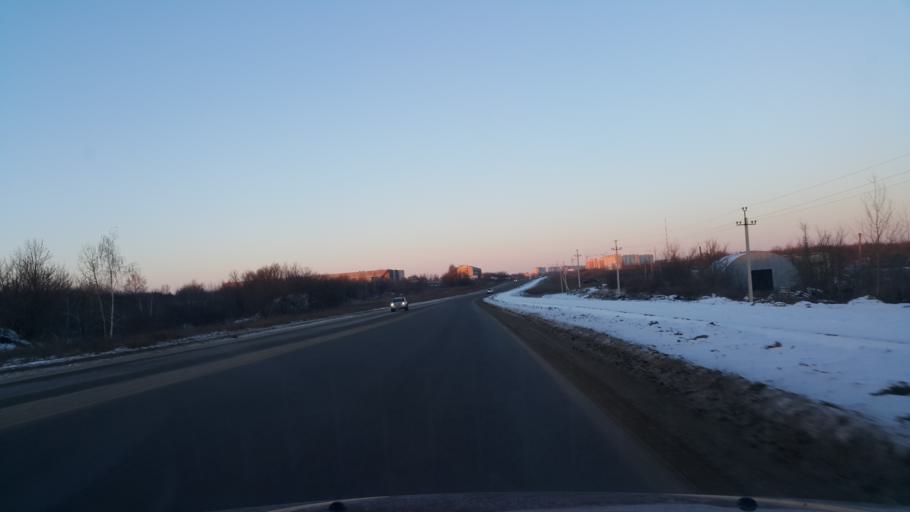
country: RU
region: Tambov
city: Tambov
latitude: 52.7416
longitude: 41.3794
